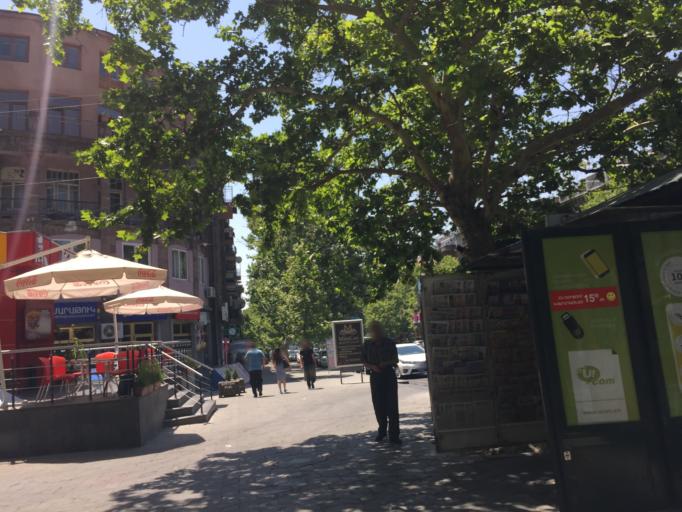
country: AM
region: Yerevan
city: Yerevan
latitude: 40.1848
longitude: 44.5125
